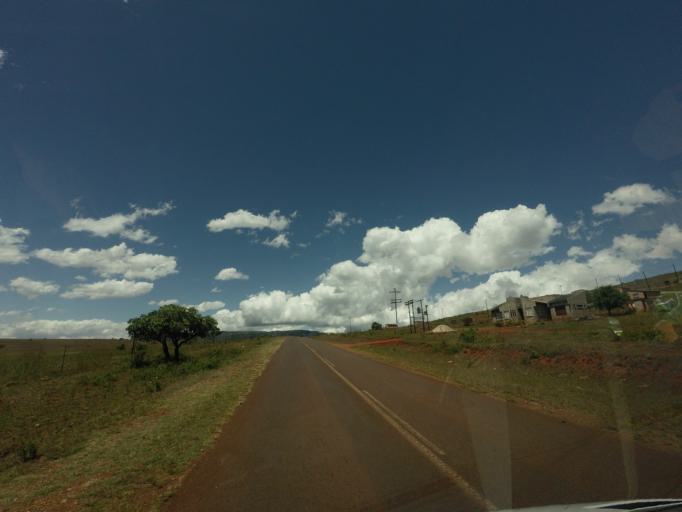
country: ZA
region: Limpopo
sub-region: Mopani District Municipality
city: Hoedspruit
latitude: -24.6088
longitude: 30.8082
